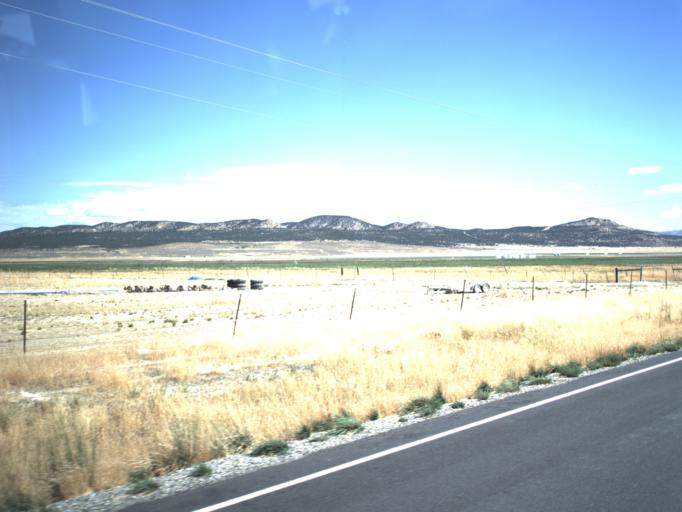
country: US
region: Idaho
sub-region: Oneida County
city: Malad City
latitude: 41.9672
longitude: -112.8445
